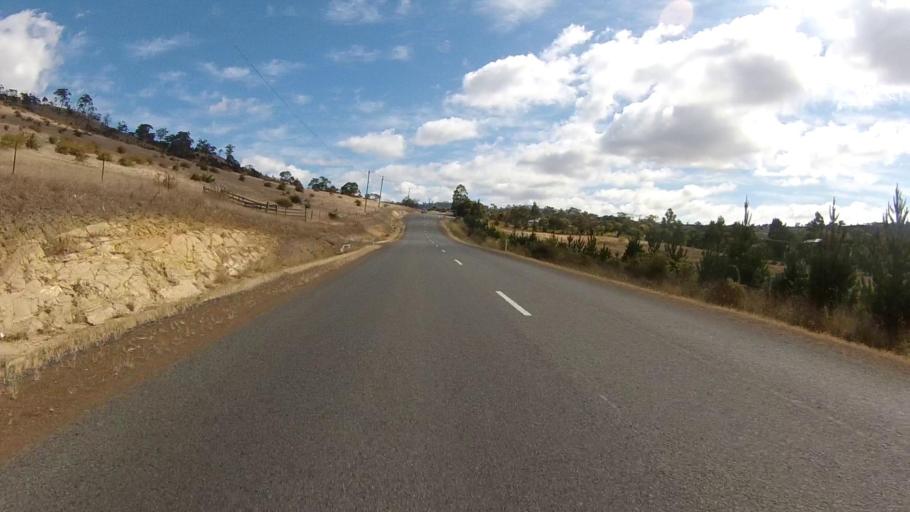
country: AU
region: Tasmania
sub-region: Brighton
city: Old Beach
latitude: -42.7386
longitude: 147.2883
